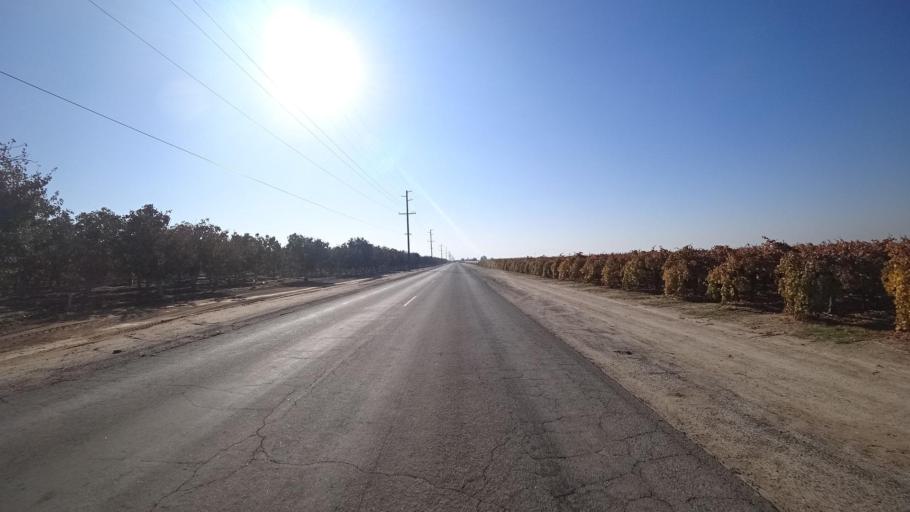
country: US
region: California
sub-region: Kern County
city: McFarland
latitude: 35.7231
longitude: -119.2051
